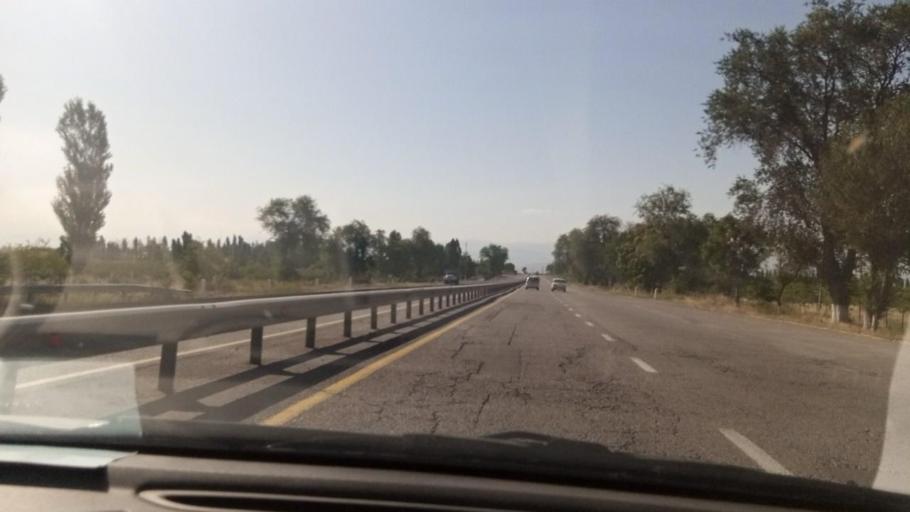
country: UZ
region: Toshkent
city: Ohangaron
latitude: 40.9374
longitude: 69.5861
